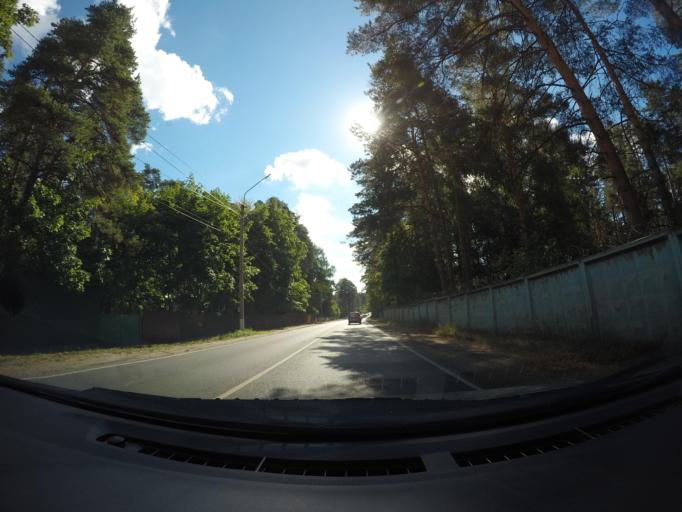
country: RU
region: Moskovskaya
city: Kratovo
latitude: 55.5966
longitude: 38.1821
